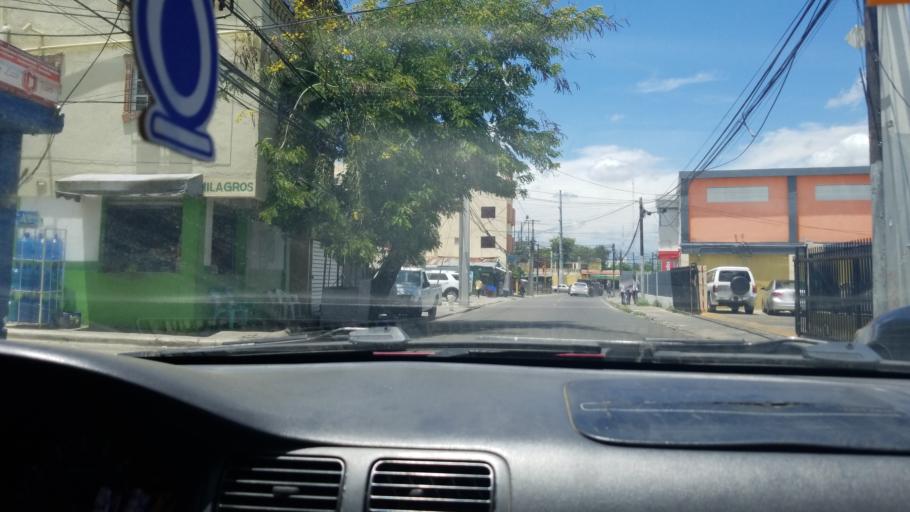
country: DO
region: Santiago
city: Santiago de los Caballeros
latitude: 19.4725
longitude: -70.6912
